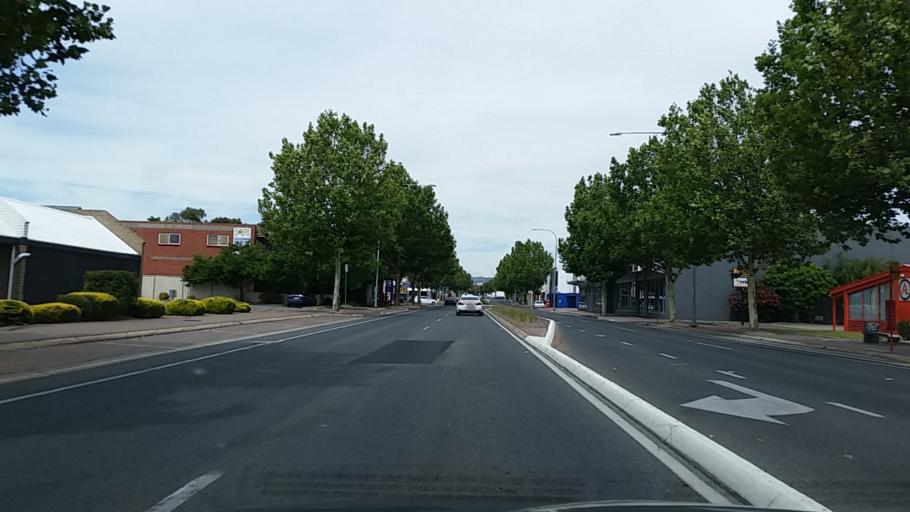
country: AU
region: South Australia
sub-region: City of West Torrens
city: Thebarton
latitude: -34.9320
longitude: 138.5659
